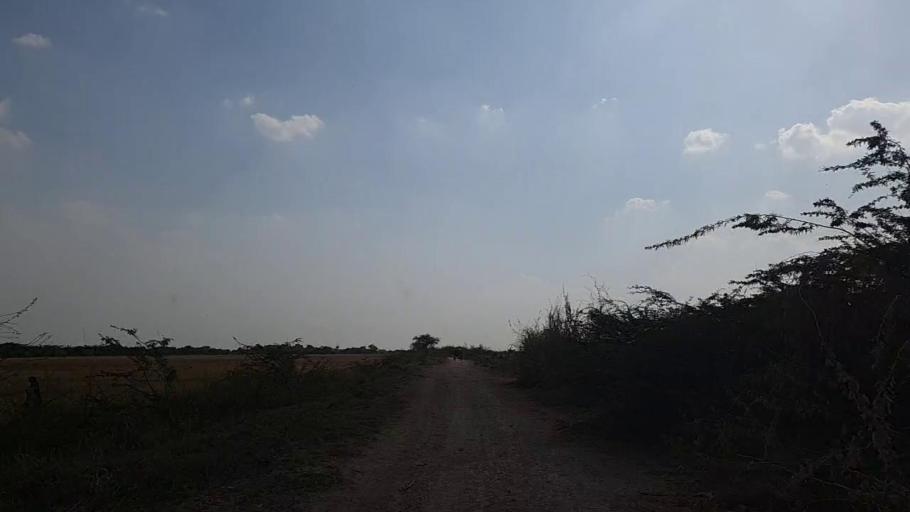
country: PK
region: Sindh
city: Jati
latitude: 24.4838
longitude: 68.3417
